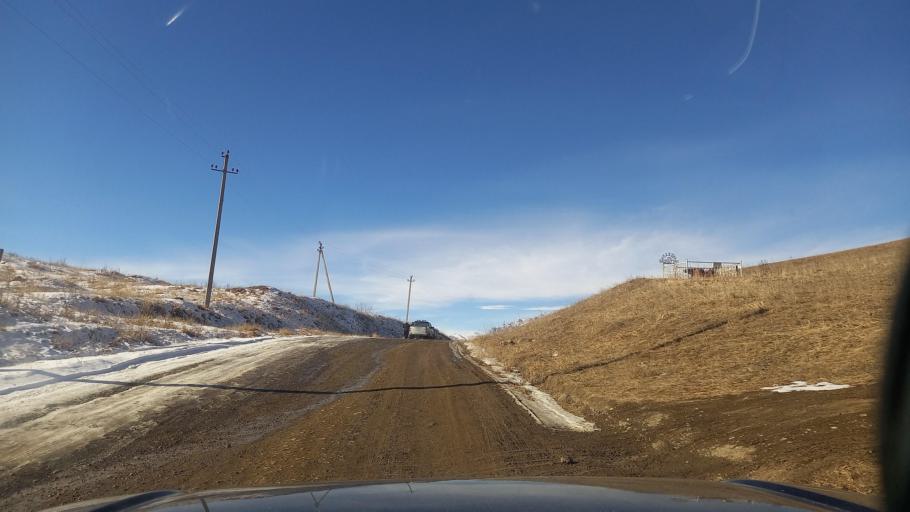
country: RU
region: North Ossetia
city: Verkhniy Fiagdon
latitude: 42.8345
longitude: 44.4797
